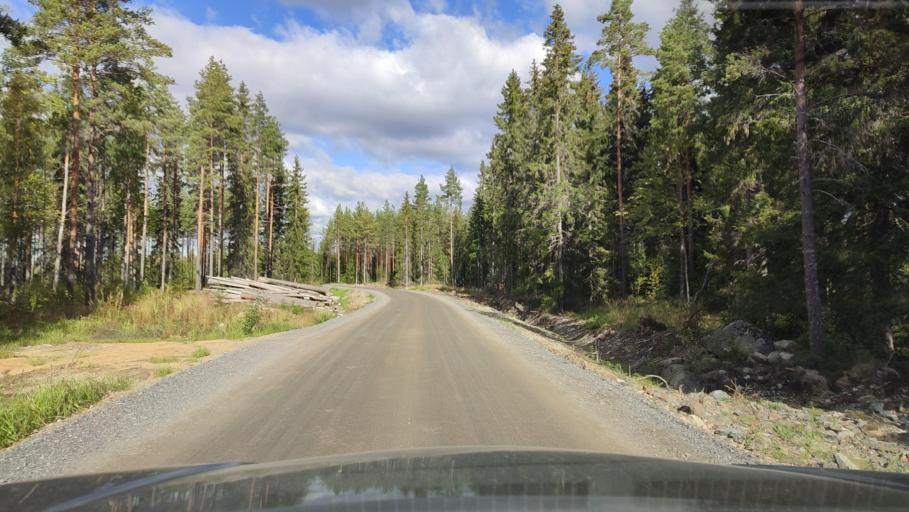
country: FI
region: Southern Ostrobothnia
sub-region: Suupohja
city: Karijoki
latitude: 62.1895
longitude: 21.5891
